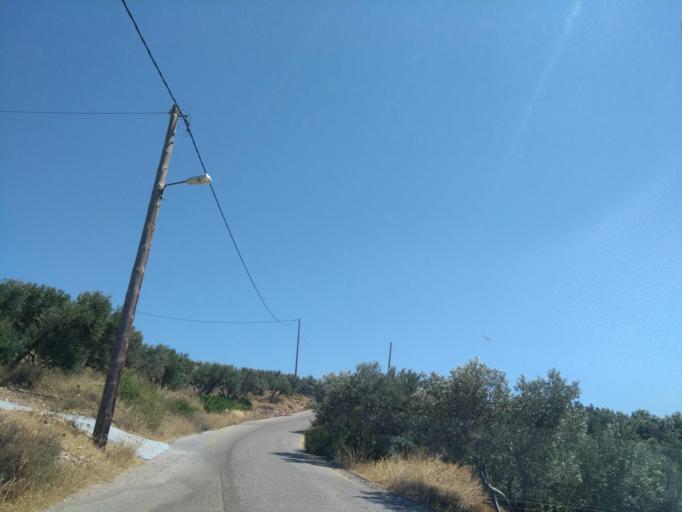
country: GR
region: Crete
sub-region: Nomos Chanias
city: Vryses
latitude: 35.3605
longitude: 23.5402
